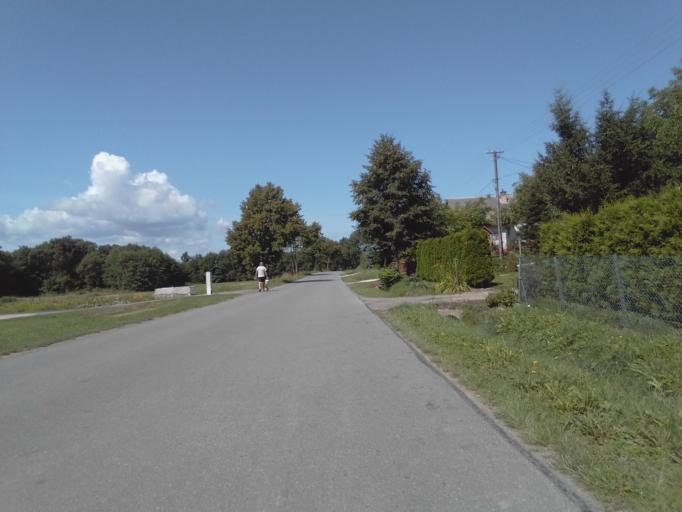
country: PL
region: Subcarpathian Voivodeship
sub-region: Powiat krosnienski
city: Chorkowka
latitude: 49.6121
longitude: 21.6079
